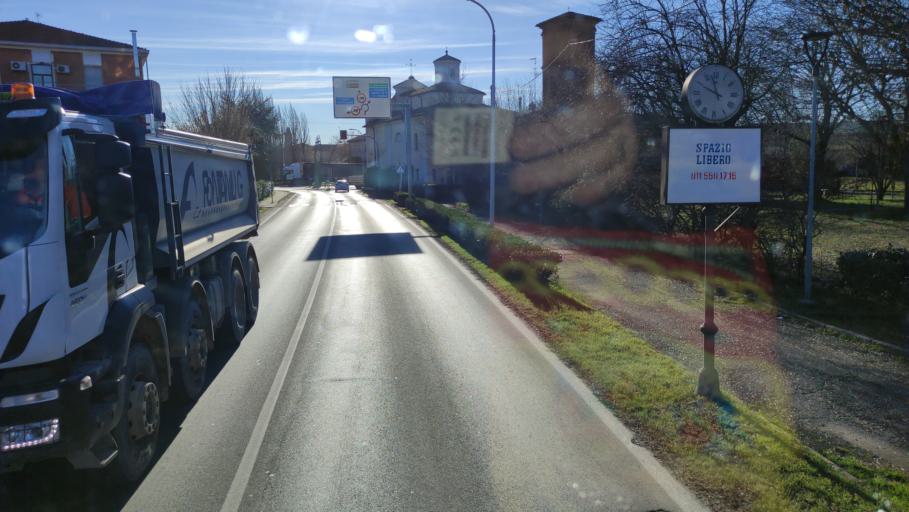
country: IT
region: Emilia-Romagna
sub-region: Provincia di Reggio Emilia
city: Novellara
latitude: 44.8501
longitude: 10.7325
